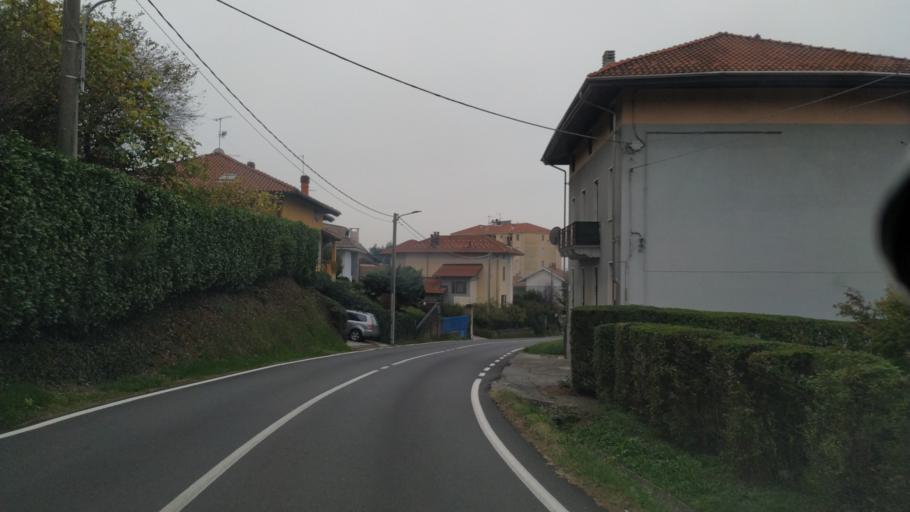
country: IT
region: Piedmont
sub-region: Provincia di Biella
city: Lessona
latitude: 45.5791
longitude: 8.1907
